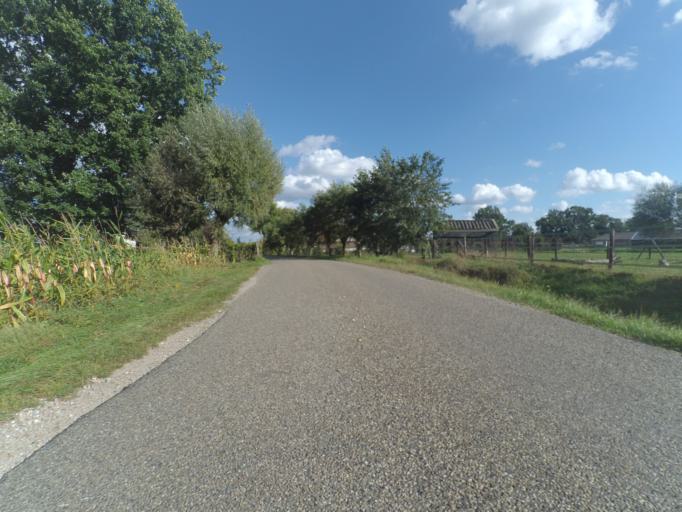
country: NL
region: Gelderland
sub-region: Gemeente Ede
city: Ederveen
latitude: 52.0722
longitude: 5.5749
